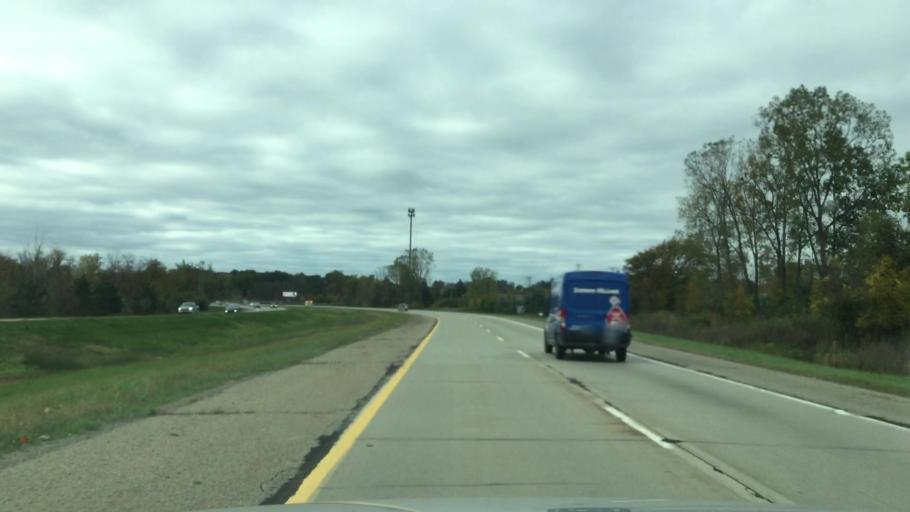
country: US
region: Michigan
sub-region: Macomb County
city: Romeo
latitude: 42.7554
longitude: -83.0161
